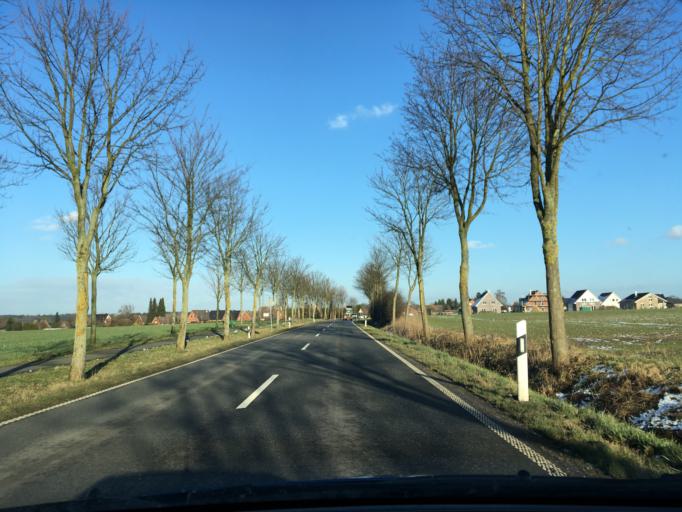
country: DE
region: Schleswig-Holstein
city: Krukow
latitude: 53.4385
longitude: 10.4792
